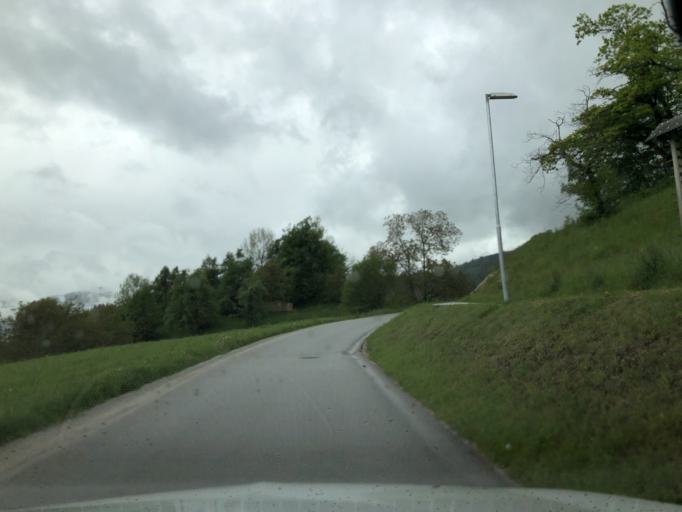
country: SI
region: Gorje
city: Zgornje Gorje
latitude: 46.3844
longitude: 14.0760
